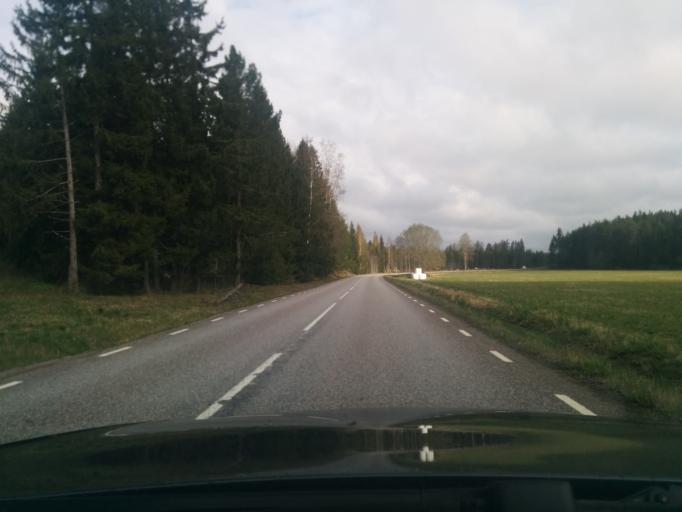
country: SE
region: Uppsala
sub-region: Tierps Kommun
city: Orbyhus
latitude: 60.2039
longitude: 17.7004
